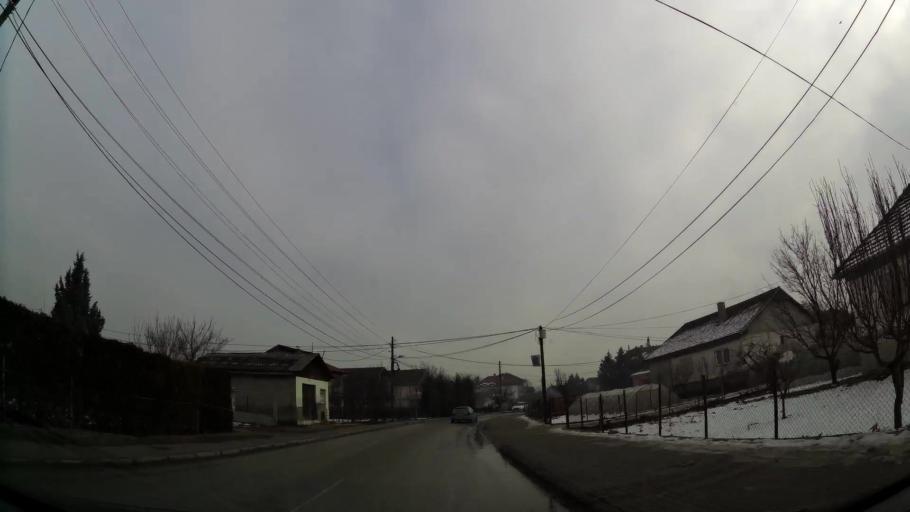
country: MK
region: Ilinden
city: Ilinden
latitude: 41.9940
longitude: 21.5792
